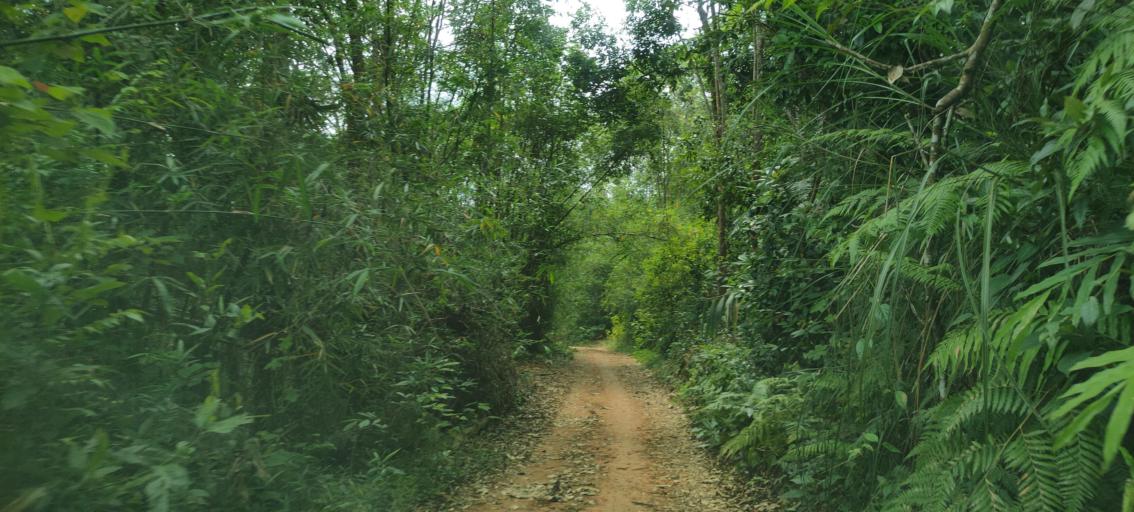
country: LA
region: Loungnamtha
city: Muang Nale
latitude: 20.4185
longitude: 101.4658
